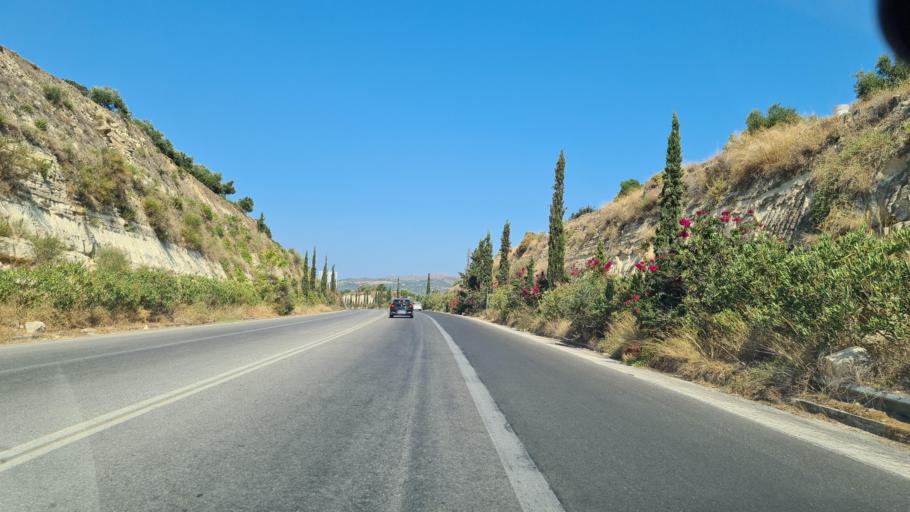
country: GR
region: Crete
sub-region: Nomos Chanias
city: Kolympari
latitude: 35.5225
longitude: 23.8129
